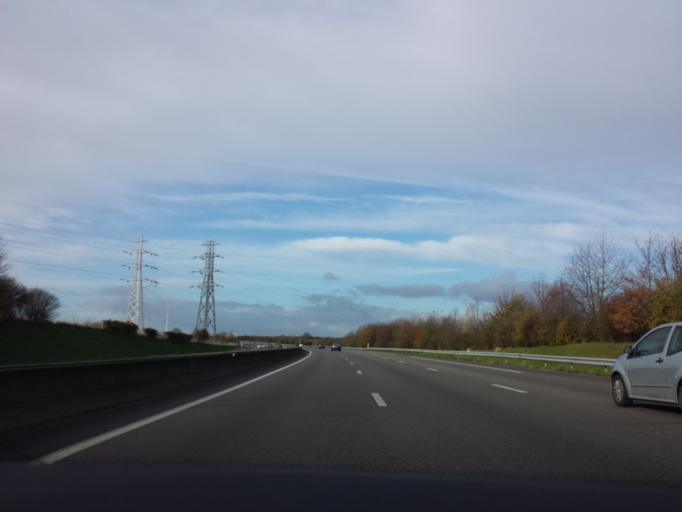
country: FR
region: Ile-de-France
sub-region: Departement des Yvelines
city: Bouafle
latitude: 48.9689
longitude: 1.9168
